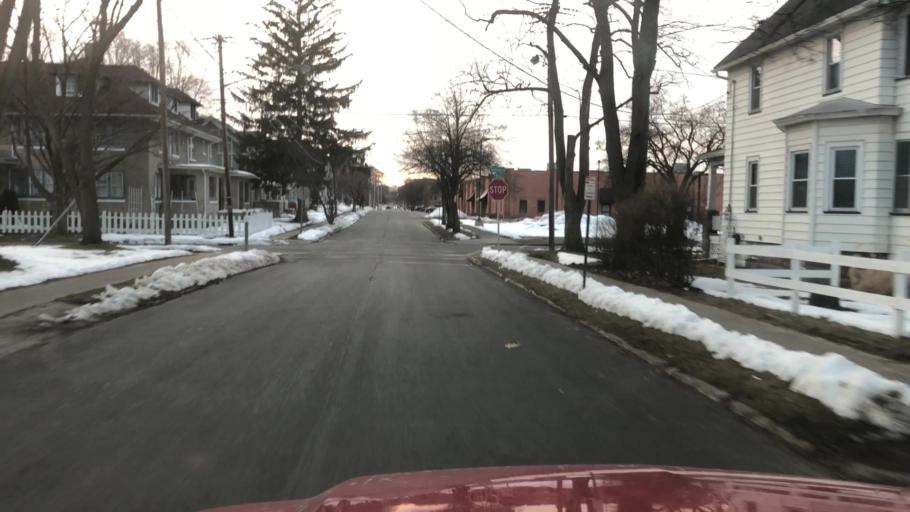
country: US
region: New York
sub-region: Monroe County
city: East Rochester
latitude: 43.1113
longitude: -77.4821
